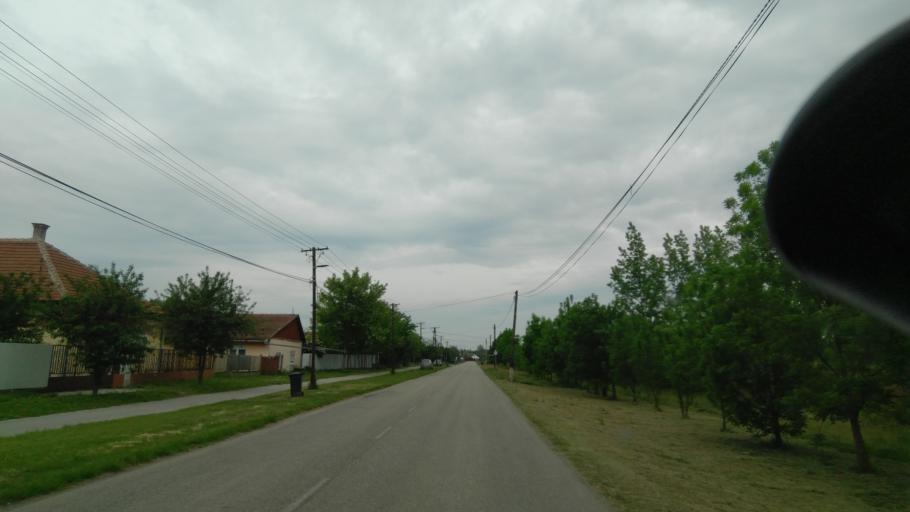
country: HU
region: Bekes
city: Veszto
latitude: 46.9176
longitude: 21.2539
